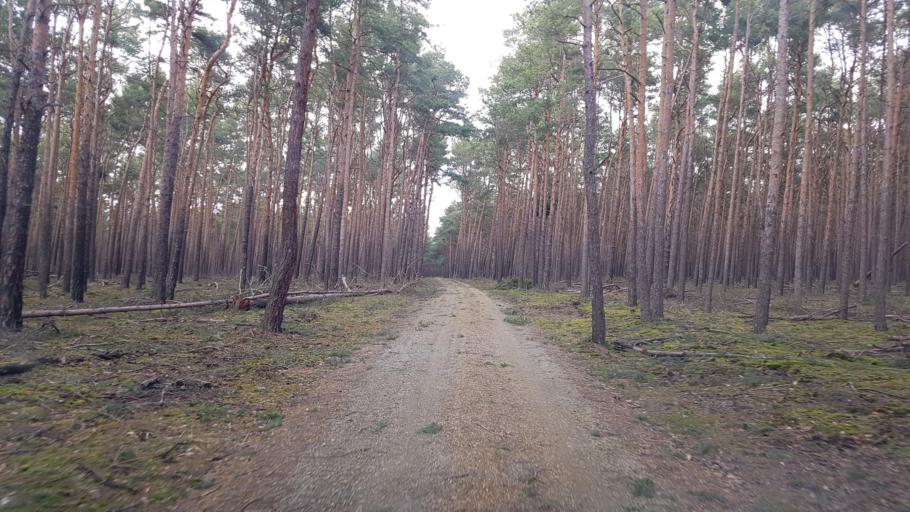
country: DE
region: Brandenburg
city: Schlieben
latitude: 51.6812
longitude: 13.4004
